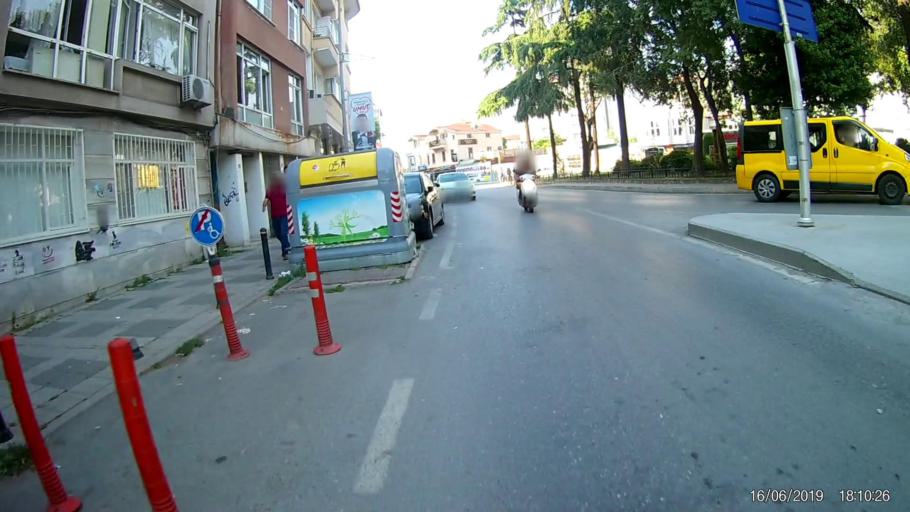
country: TR
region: Istanbul
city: UEskuedar
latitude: 40.9868
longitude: 29.0335
